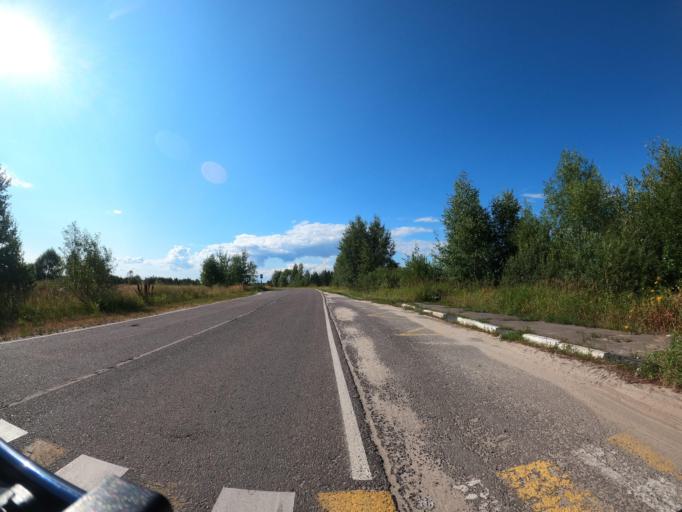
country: RU
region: Moskovskaya
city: Konobeyevo
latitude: 55.3975
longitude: 38.7164
